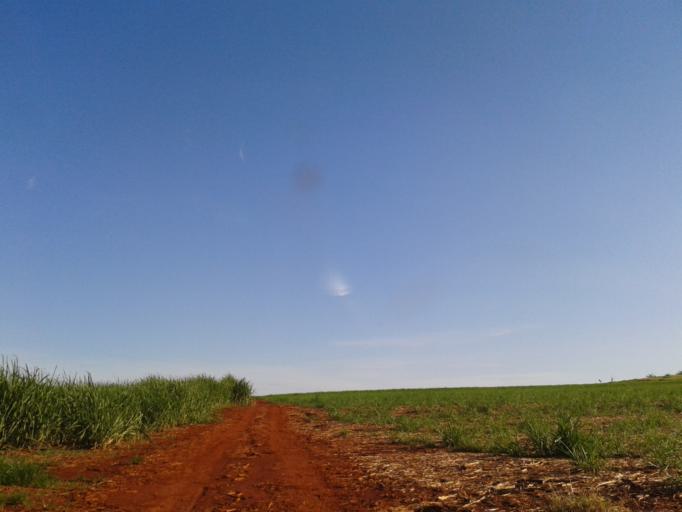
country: BR
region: Minas Gerais
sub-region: Centralina
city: Centralina
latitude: -18.6711
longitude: -49.2714
